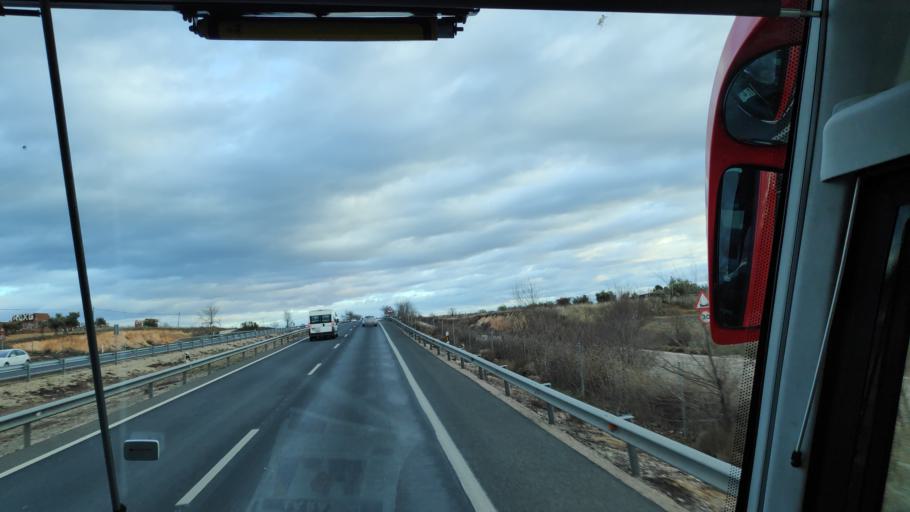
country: ES
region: Madrid
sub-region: Provincia de Madrid
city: Villarejo de Salvanes
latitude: 40.1595
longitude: -3.2619
